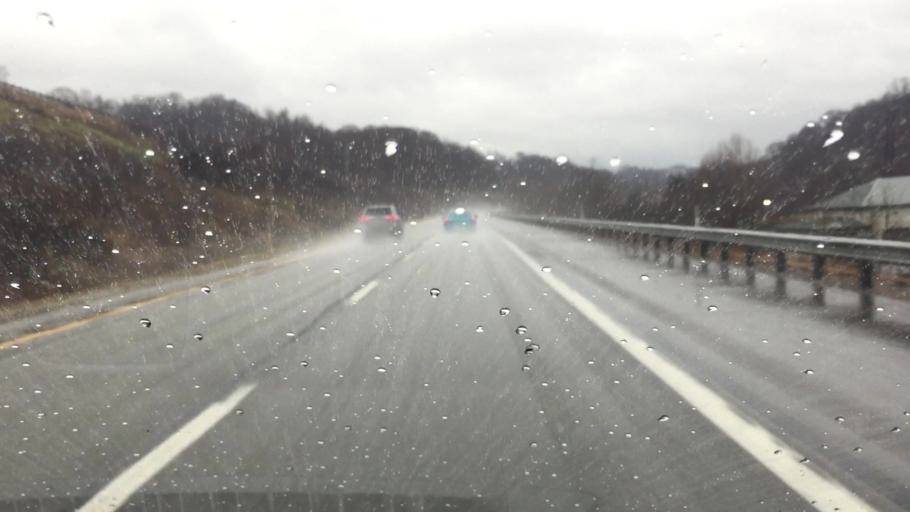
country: US
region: Pennsylvania
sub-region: Allegheny County
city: Ben Avon
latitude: 40.5368
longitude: -80.0766
